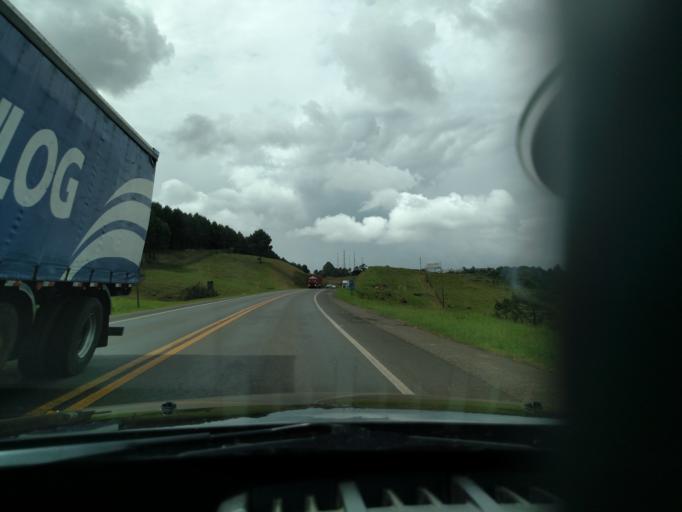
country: BR
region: Santa Catarina
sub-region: Lages
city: Lages
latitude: -27.8271
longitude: -50.3799
